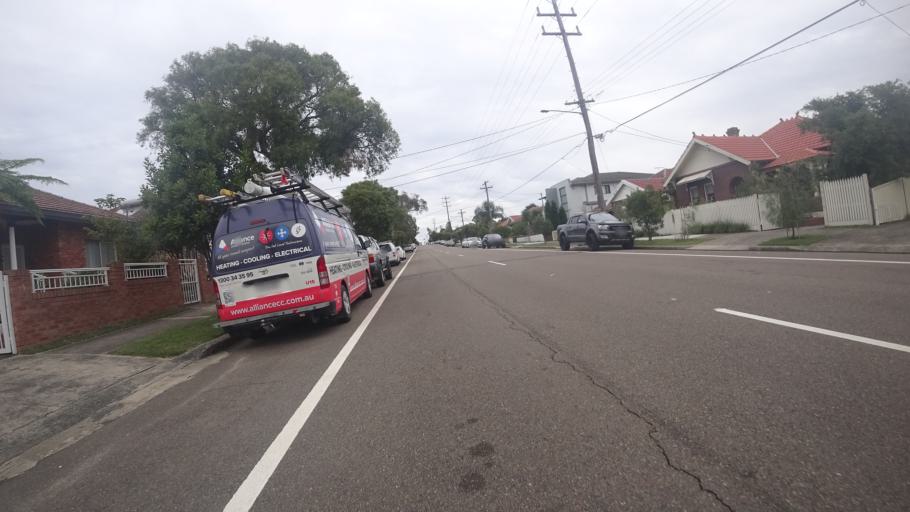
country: AU
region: New South Wales
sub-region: Rockdale
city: Bardwell Valley
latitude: -33.9378
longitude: 151.1350
